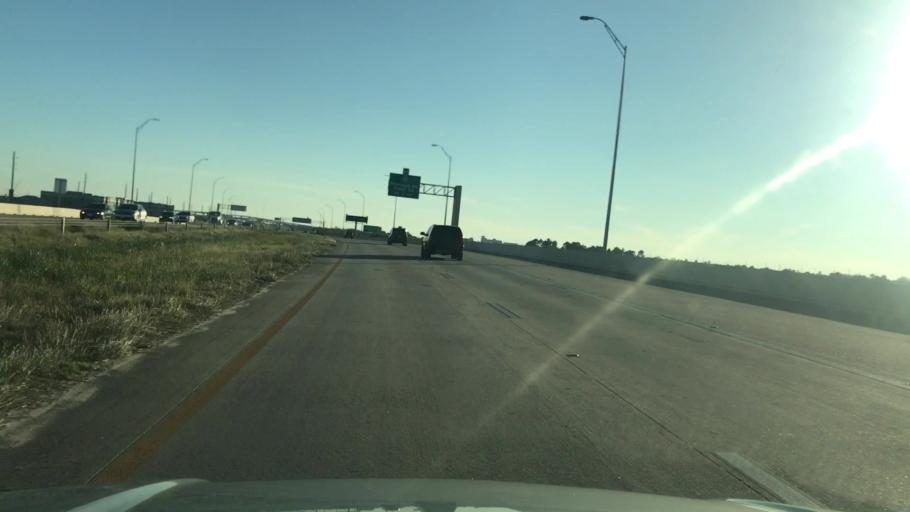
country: US
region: Texas
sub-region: Harris County
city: Katy
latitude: 29.8128
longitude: -95.7734
